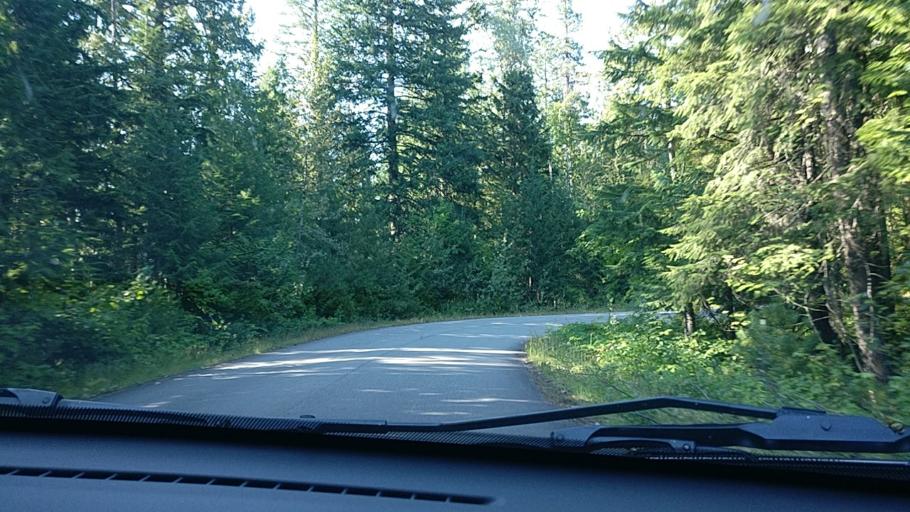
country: CA
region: British Columbia
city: Revelstoke
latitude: 51.0211
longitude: -118.2010
